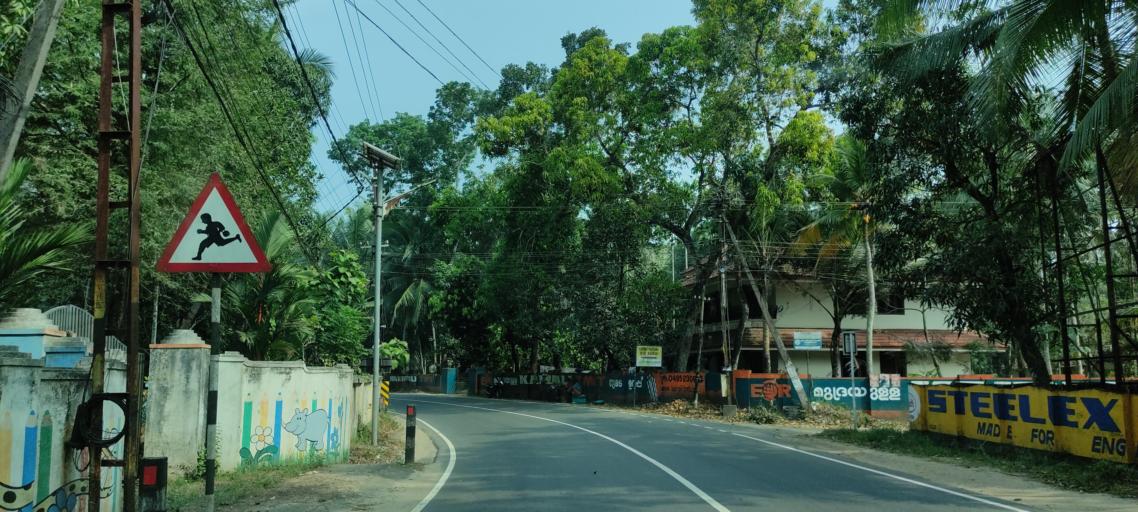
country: IN
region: Kerala
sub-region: Kottayam
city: Vaikam
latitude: 9.7583
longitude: 76.4052
